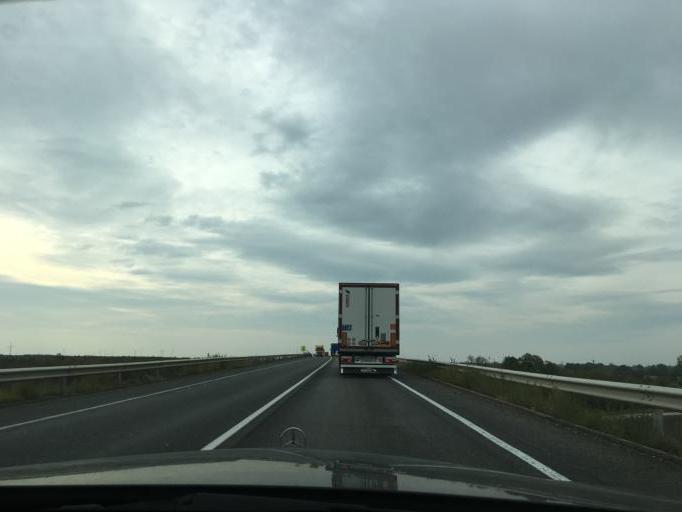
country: HU
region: Gyor-Moson-Sopron
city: Rajka
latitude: 47.9374
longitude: 17.1673
